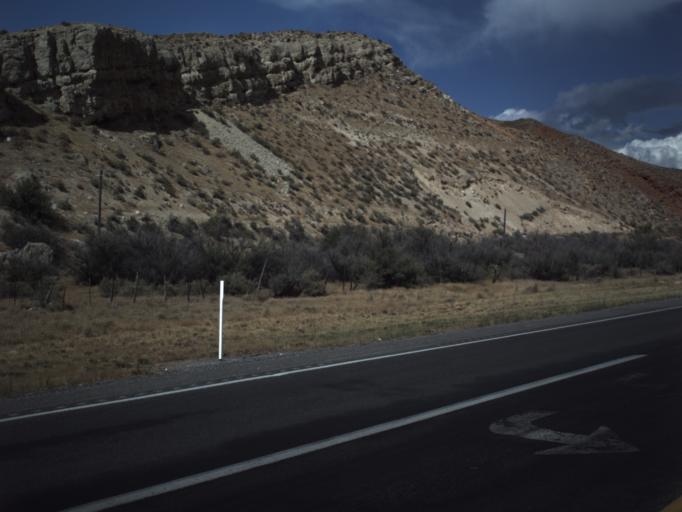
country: US
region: Utah
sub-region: Sanpete County
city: Gunnison
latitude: 39.1598
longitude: -111.7502
